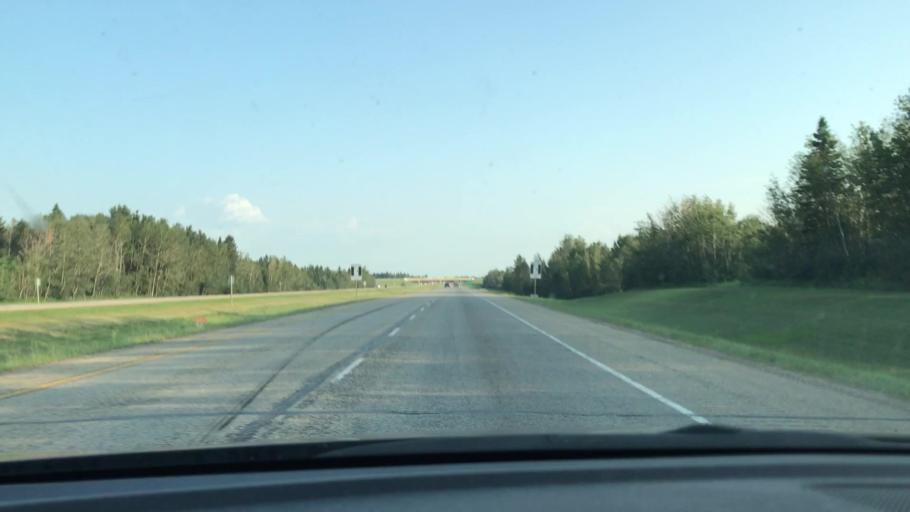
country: CA
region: Alberta
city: Lacombe
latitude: 52.5680
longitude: -113.6631
